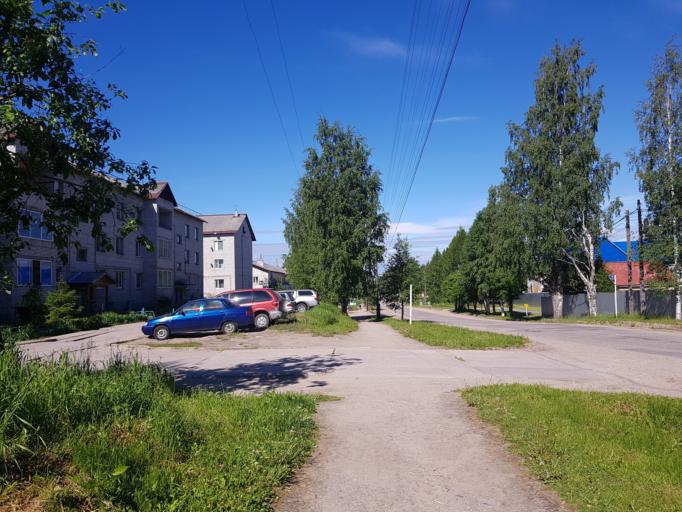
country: RU
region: Republic of Karelia
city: Kalevala
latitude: 65.1960
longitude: 31.2042
